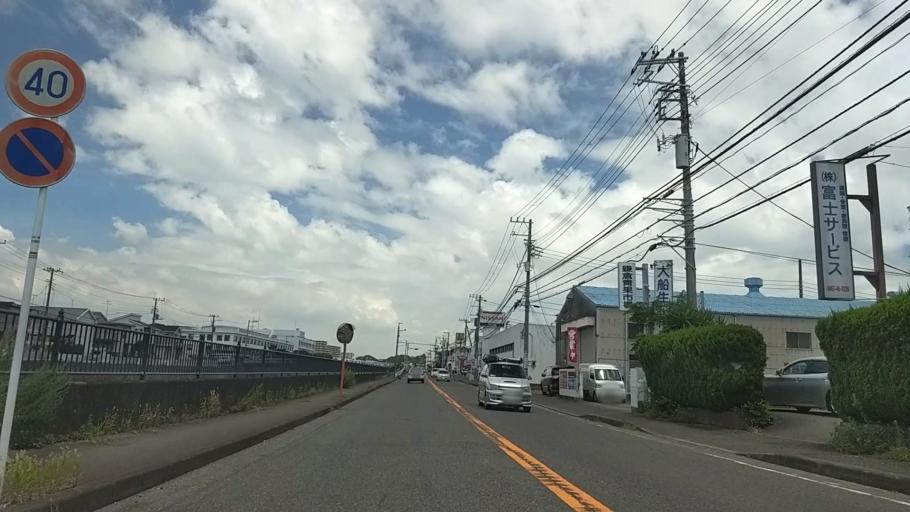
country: JP
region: Kanagawa
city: Fujisawa
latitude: 35.3345
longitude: 139.5110
